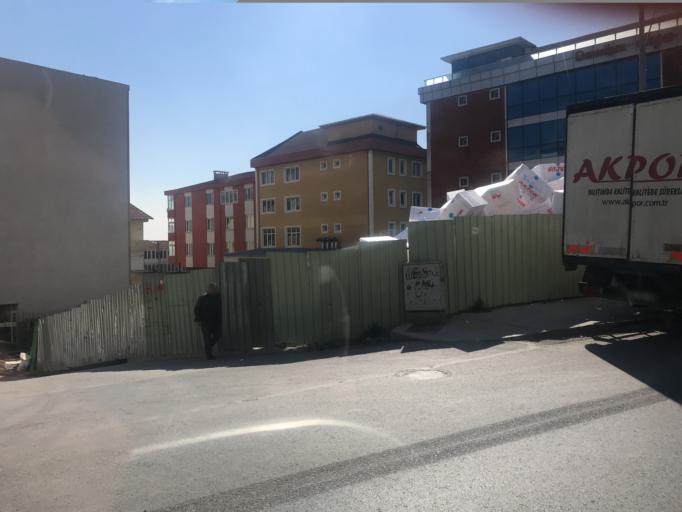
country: TR
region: Istanbul
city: Pendik
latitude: 40.8978
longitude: 29.2545
